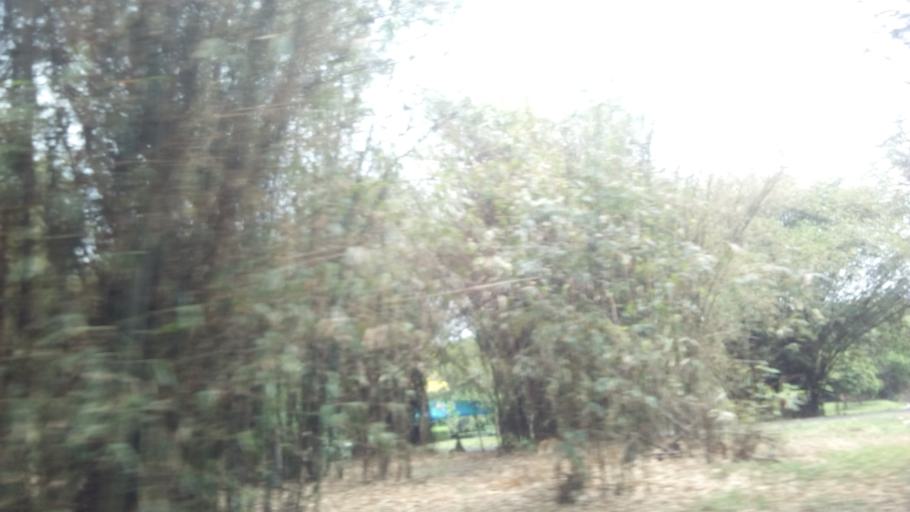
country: TH
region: Nakhon Pathom
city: Salaya
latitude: 13.7830
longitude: 100.3107
